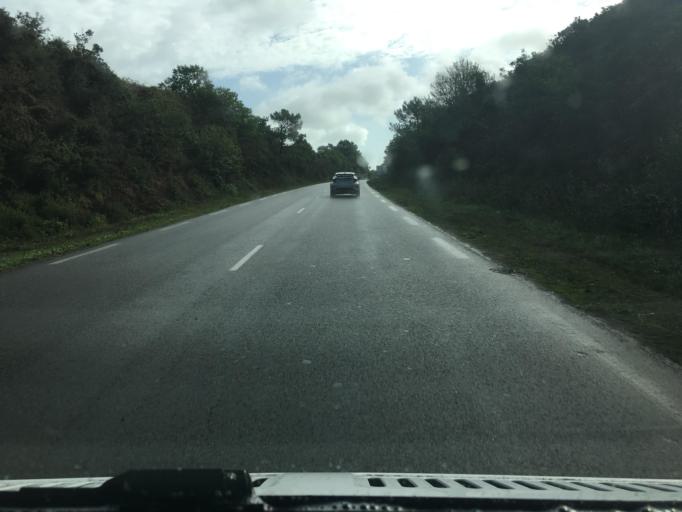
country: FR
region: Brittany
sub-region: Departement du Finistere
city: Ploneour-Lanvern
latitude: 47.8802
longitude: -4.2239
